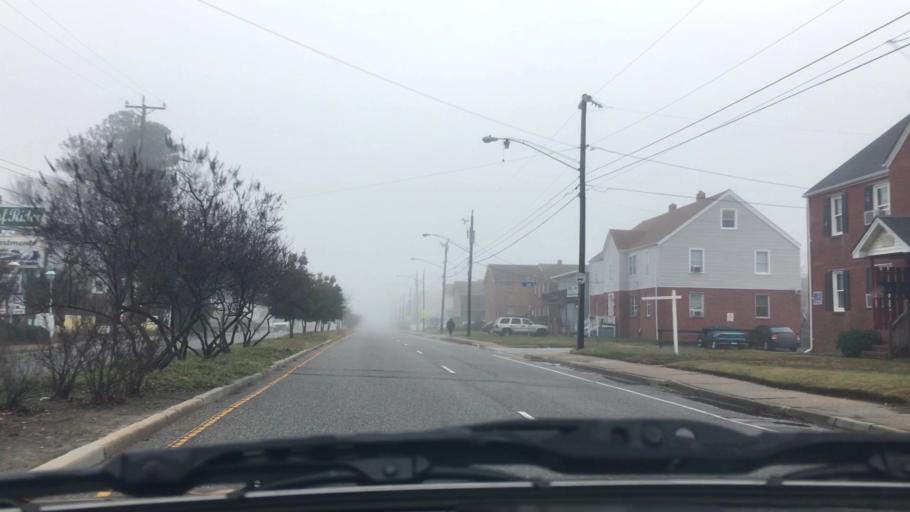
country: US
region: Virginia
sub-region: City of Hampton
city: East Hampton
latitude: 36.9671
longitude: -76.2864
